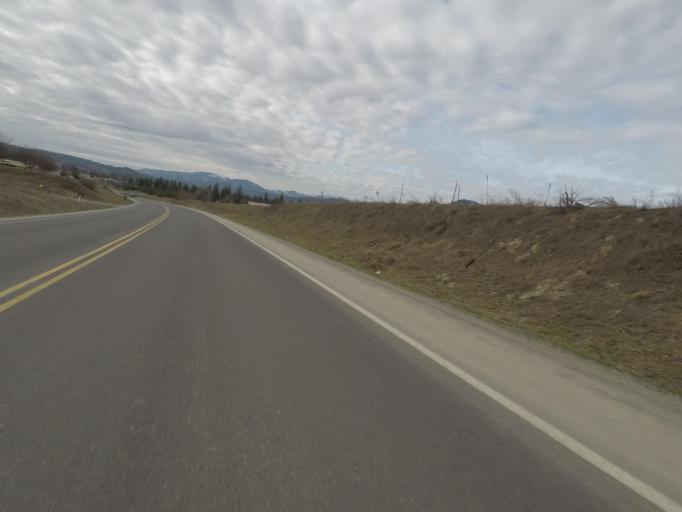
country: US
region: Washington
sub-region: Stevens County
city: Colville
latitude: 48.5557
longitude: -117.8819
